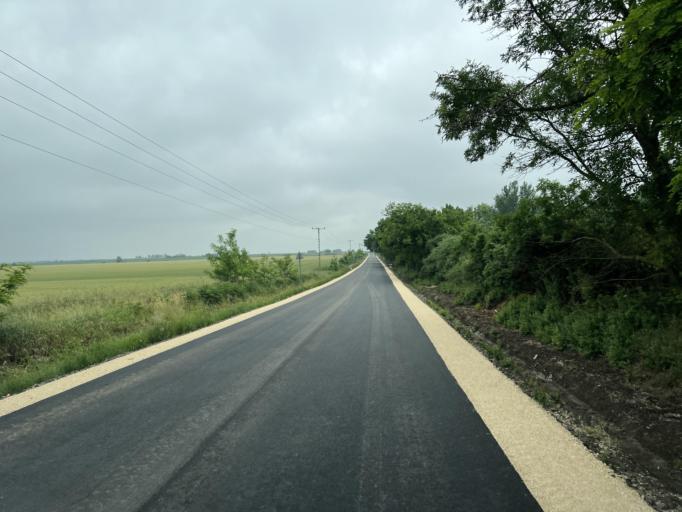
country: HU
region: Pest
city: Vacszentlaszlo
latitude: 47.5861
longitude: 19.5657
